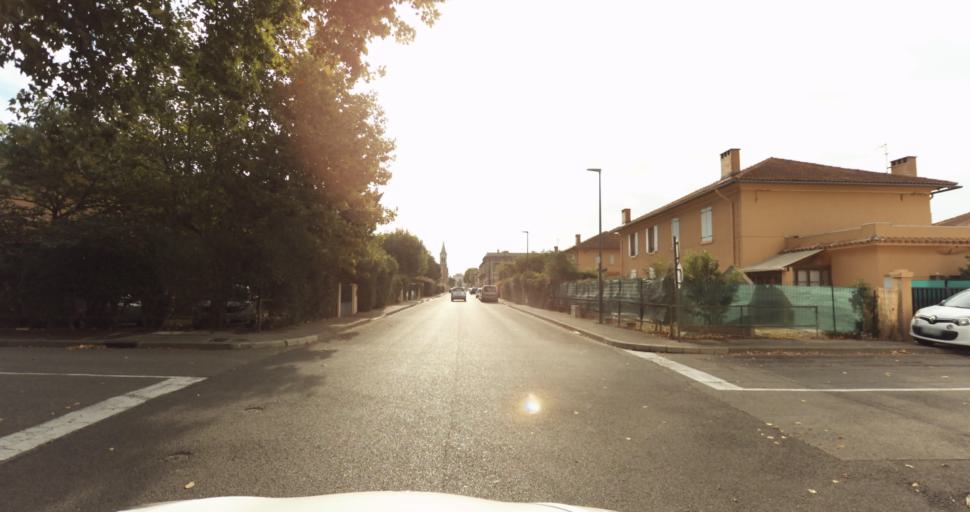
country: FR
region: Provence-Alpes-Cote d'Azur
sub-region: Departement des Bouches-du-Rhone
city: Miramas
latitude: 43.5832
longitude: 4.9974
